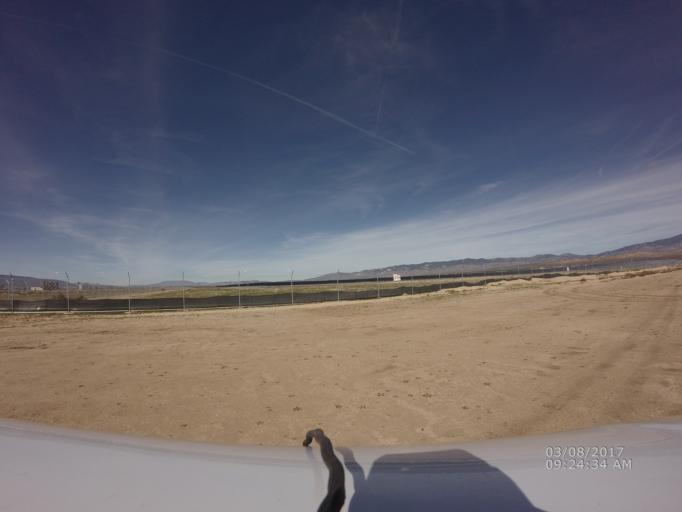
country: US
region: California
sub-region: Los Angeles County
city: Green Valley
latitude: 34.8186
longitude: -118.4669
